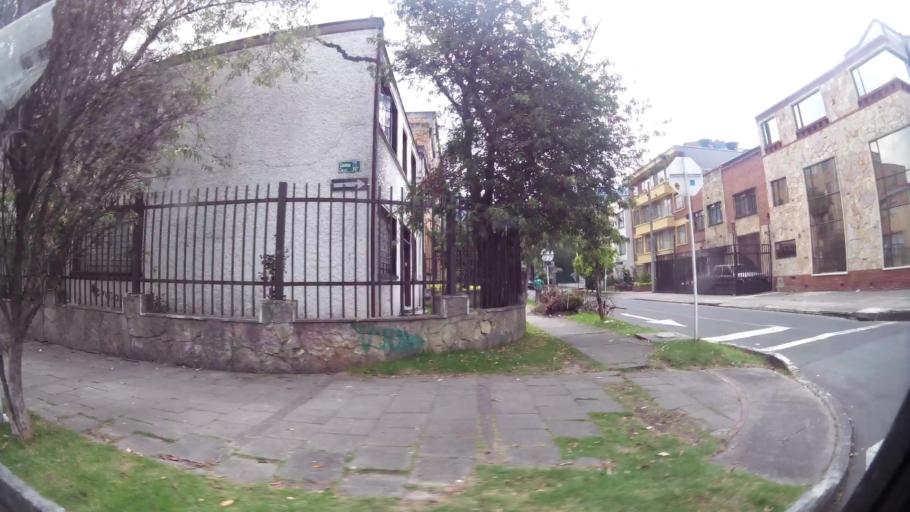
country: CO
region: Bogota D.C.
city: Bogota
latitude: 4.6294
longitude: -74.0740
